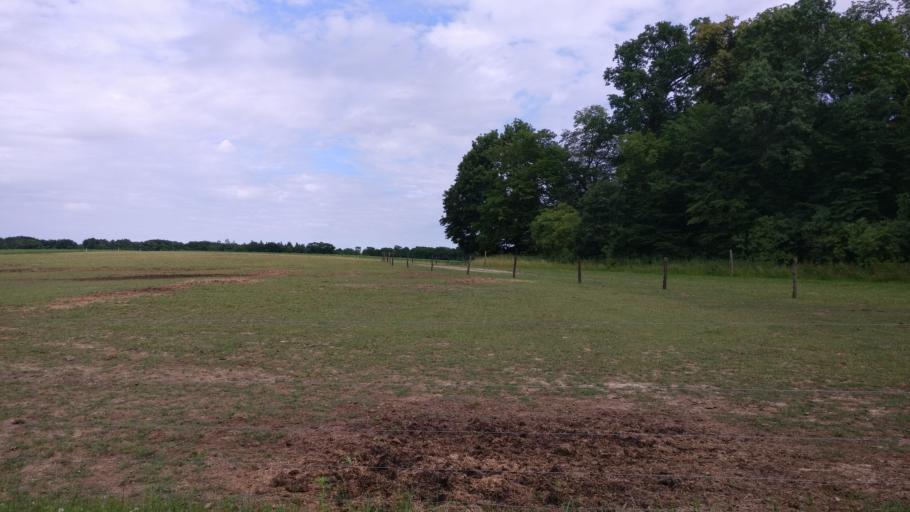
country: DE
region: Brandenburg
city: Briesen
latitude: 52.3892
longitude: 14.2823
